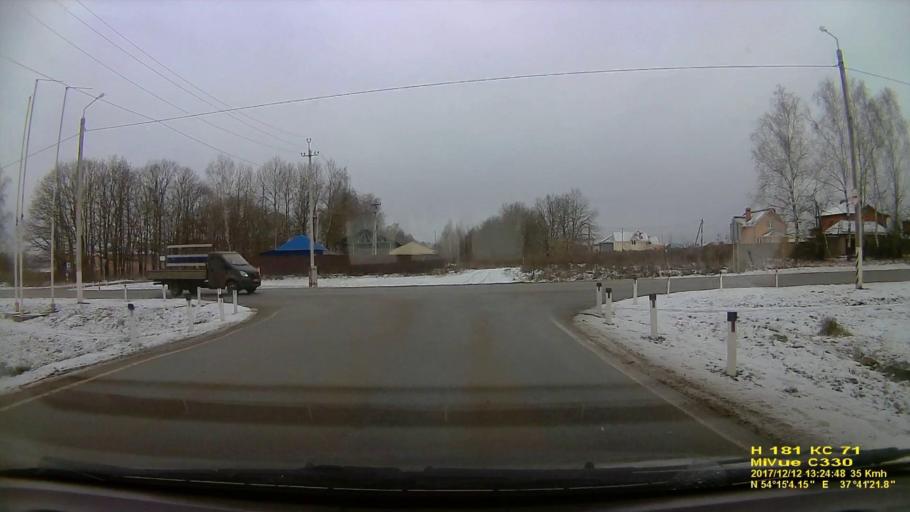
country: RU
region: Tula
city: Gorelki
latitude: 54.2523
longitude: 37.6893
